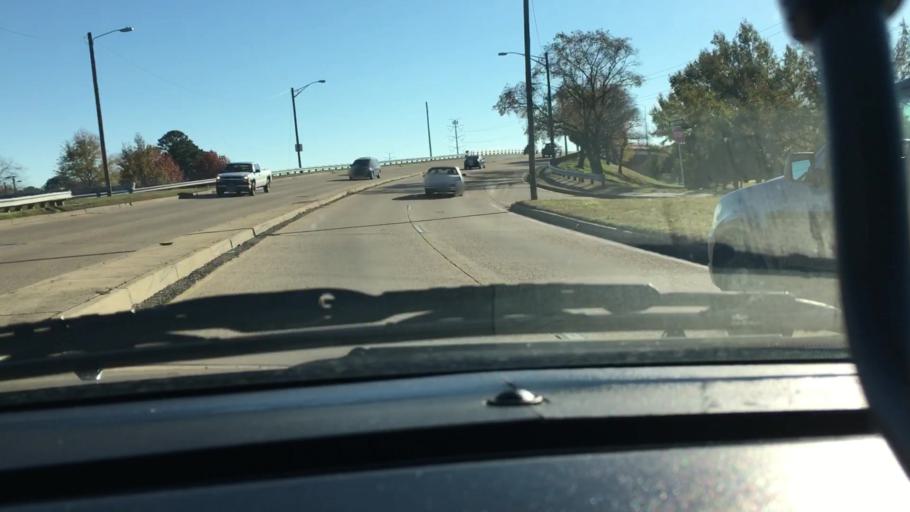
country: US
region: Virginia
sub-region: City of Norfolk
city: Norfolk
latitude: 36.8990
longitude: -76.2557
